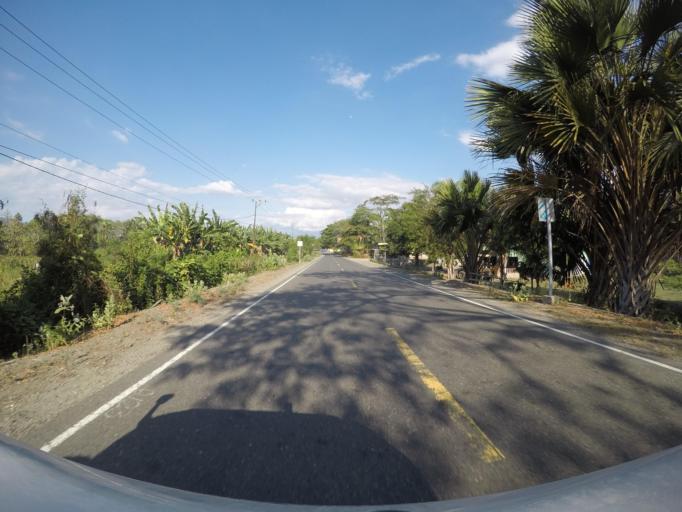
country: TL
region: Liquica
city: Maubara
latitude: -8.7292
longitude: 125.1205
